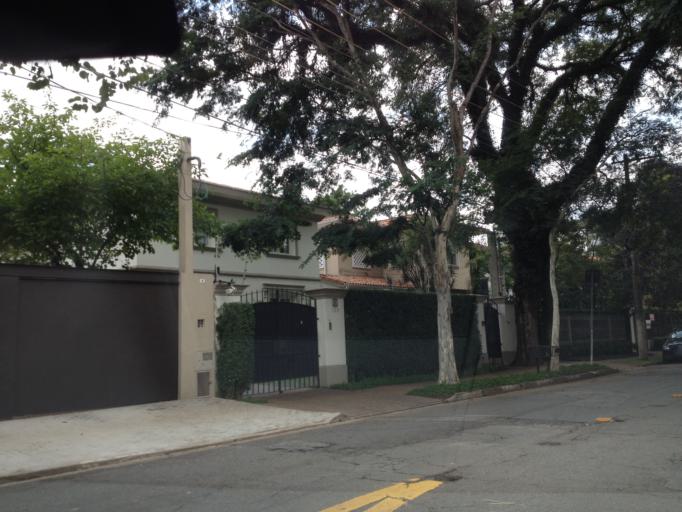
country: BR
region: Sao Paulo
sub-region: Sao Paulo
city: Sao Paulo
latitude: -23.5589
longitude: -46.6940
